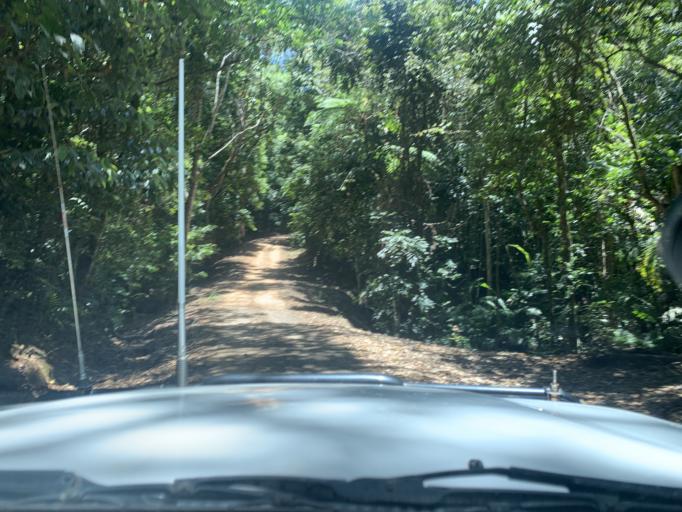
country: AU
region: Queensland
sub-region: Cairns
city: Redlynch
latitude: -16.9586
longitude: 145.6432
